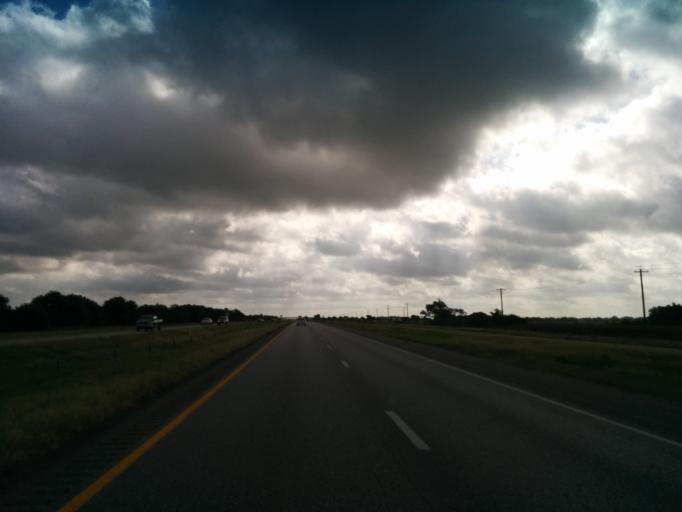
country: US
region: Texas
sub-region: Guadalupe County
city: Marion
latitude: 29.5136
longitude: -98.1531
